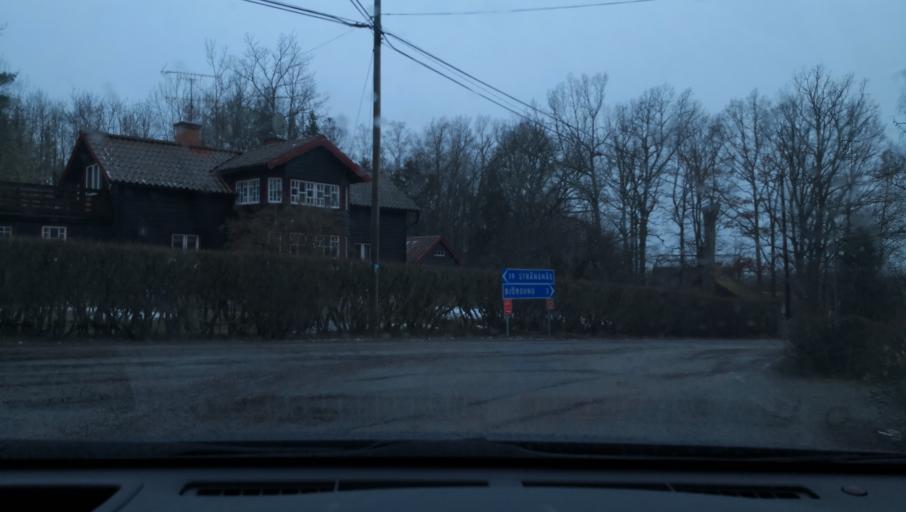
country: SE
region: Soedermanland
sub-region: Eskilstuna Kommun
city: Arla
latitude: 59.4467
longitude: 16.7788
